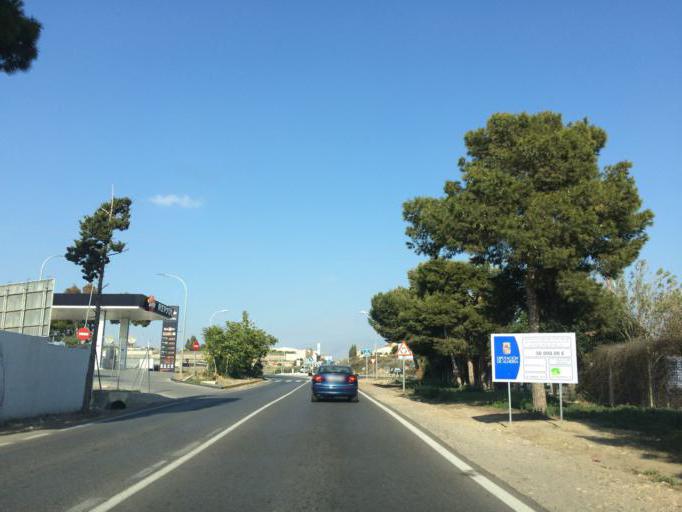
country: ES
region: Andalusia
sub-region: Provincia de Almeria
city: Huercal de Almeria
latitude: 36.8530
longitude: -2.4205
